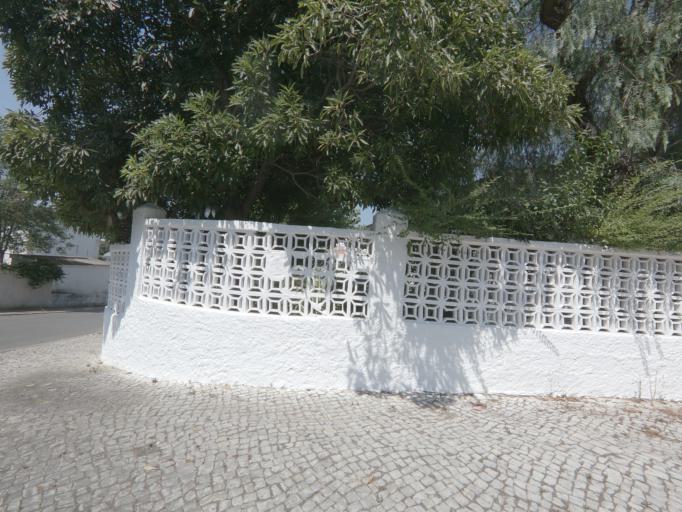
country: PT
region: Setubal
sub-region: Setubal
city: Setubal
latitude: 38.5450
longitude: -8.8836
